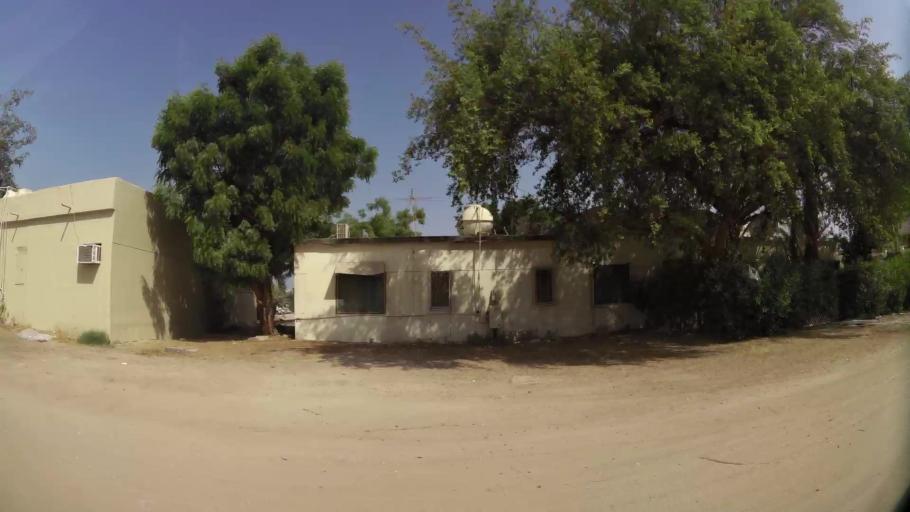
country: AE
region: Ash Shariqah
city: Sharjah
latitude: 25.3432
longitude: 55.4158
